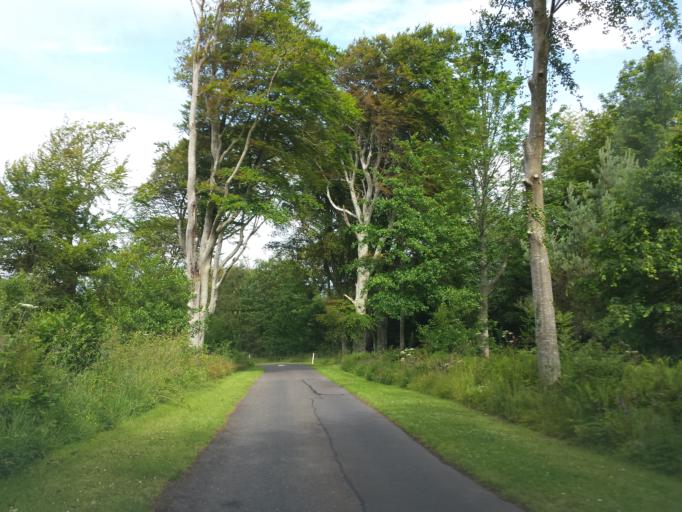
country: GB
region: Scotland
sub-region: South Ayrshire
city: Maybole
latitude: 55.3537
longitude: -4.7794
